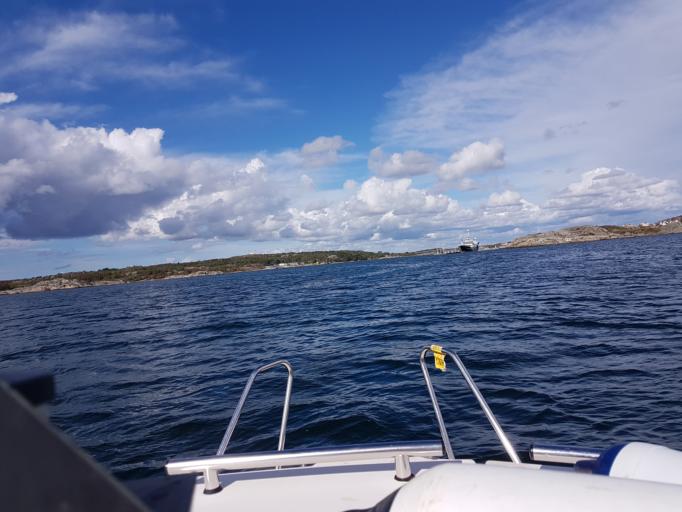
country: SE
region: Vaestra Goetaland
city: Donso
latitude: 57.5932
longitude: 11.7847
